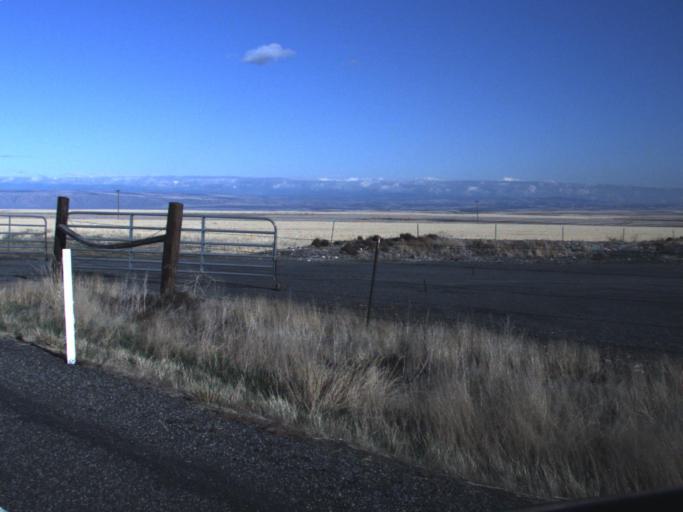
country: US
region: Washington
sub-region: Asotin County
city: Asotin
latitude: 46.2062
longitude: -117.0704
